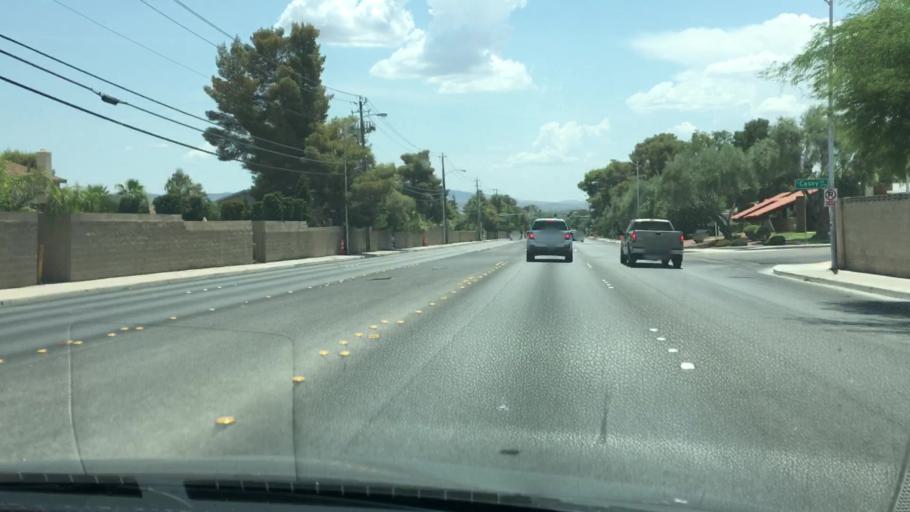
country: US
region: Nevada
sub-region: Clark County
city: Whitney
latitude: 36.0953
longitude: -115.0917
